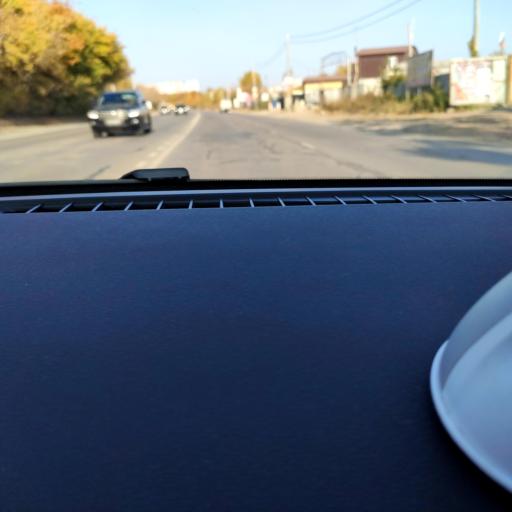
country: RU
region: Samara
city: Petra-Dubrava
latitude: 53.2692
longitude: 50.2790
